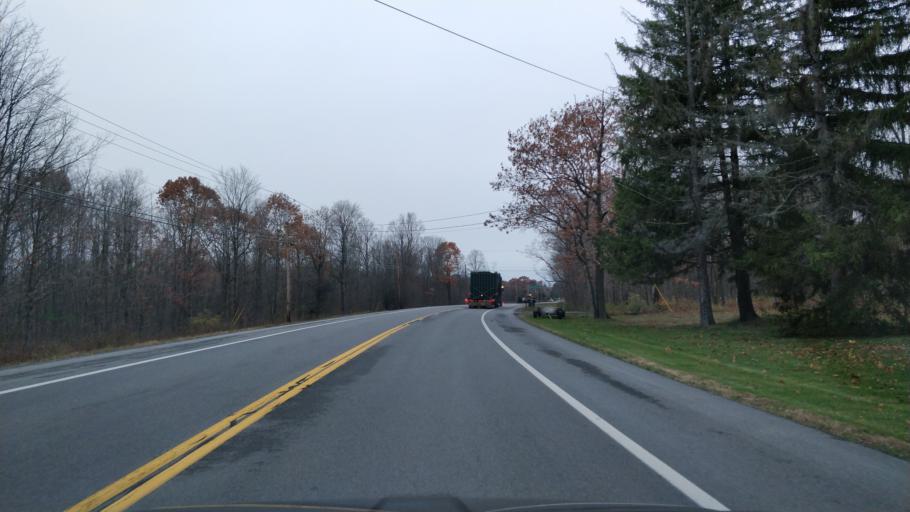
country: CA
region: Ontario
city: Brockville
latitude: 44.6013
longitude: -75.6244
